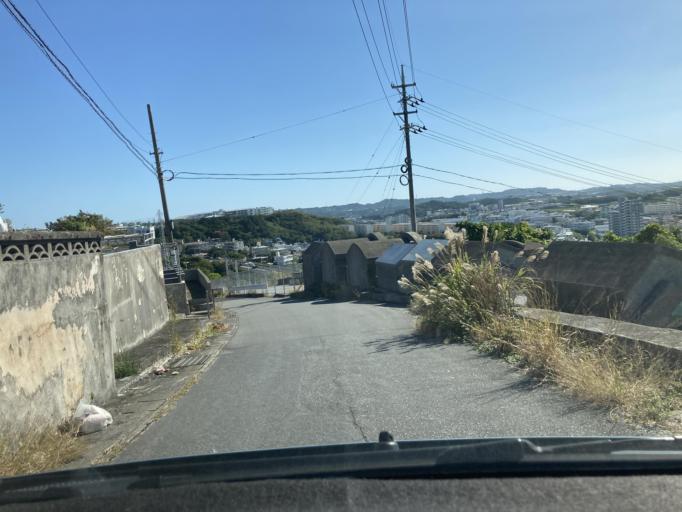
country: JP
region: Okinawa
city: Naha-shi
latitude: 26.2031
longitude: 127.7135
